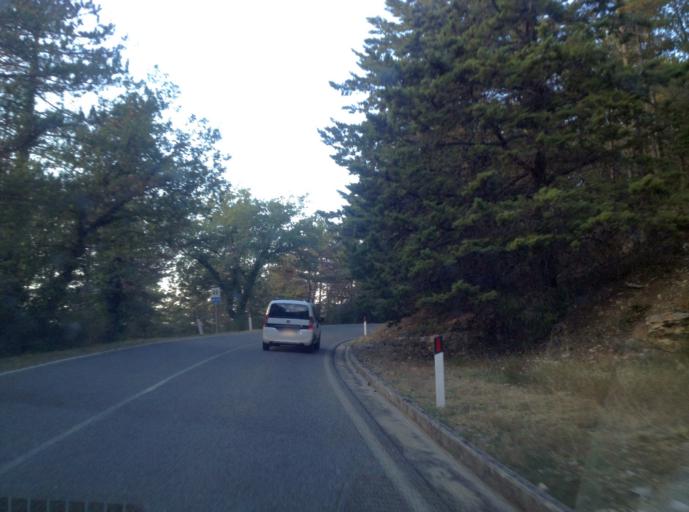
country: IT
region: Tuscany
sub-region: Provincia di Siena
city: Castellina in Chianti
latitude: 43.4315
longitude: 11.3099
